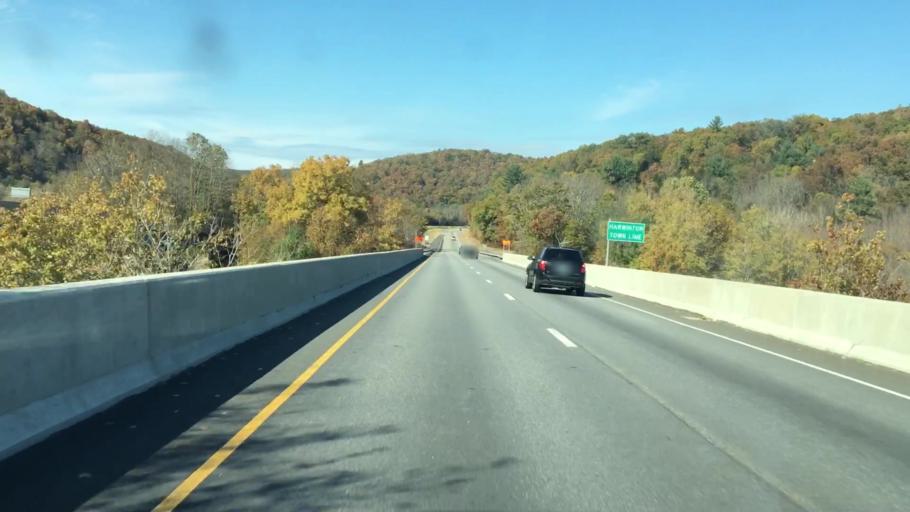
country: US
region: Connecticut
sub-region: Litchfield County
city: Northwest Harwinton
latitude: 41.7385
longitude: -73.1106
